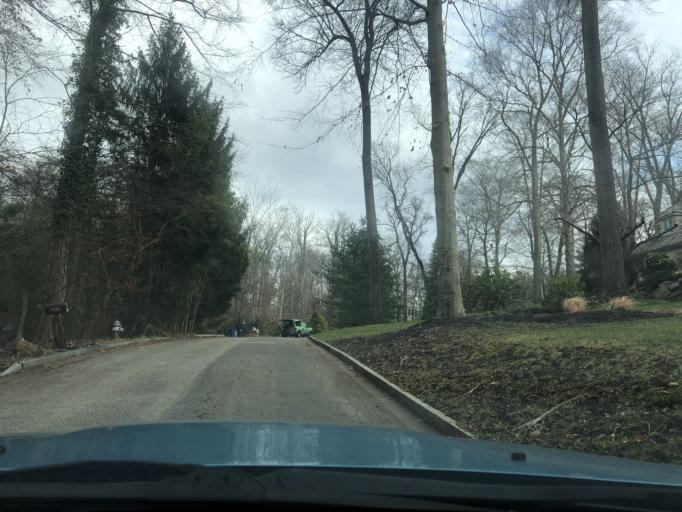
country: US
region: Pennsylvania
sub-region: Delaware County
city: Radnor
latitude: 40.0340
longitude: -75.3630
